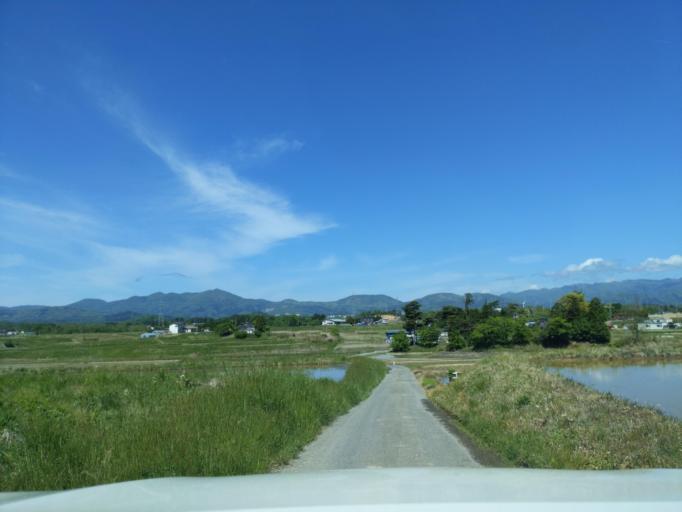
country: JP
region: Fukushima
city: Koriyama
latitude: 37.4388
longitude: 140.3338
